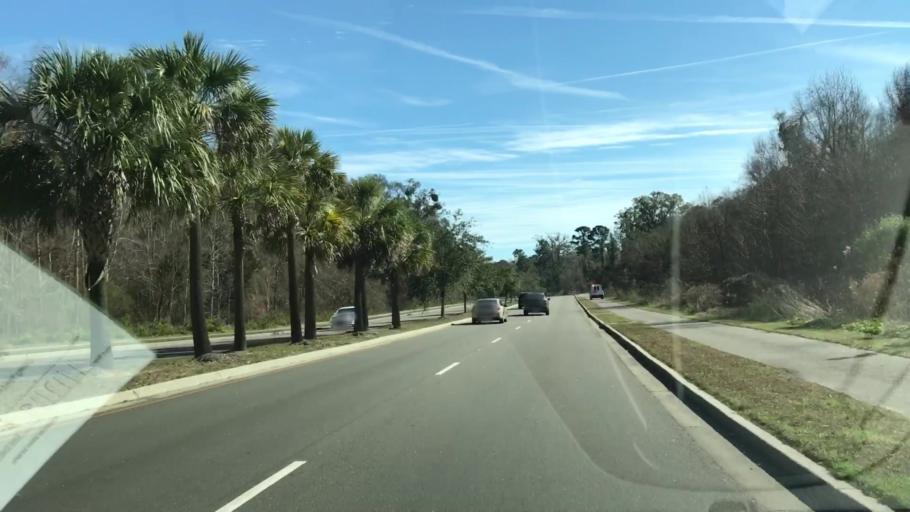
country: US
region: South Carolina
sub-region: Beaufort County
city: Bluffton
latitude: 32.2641
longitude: -80.8784
